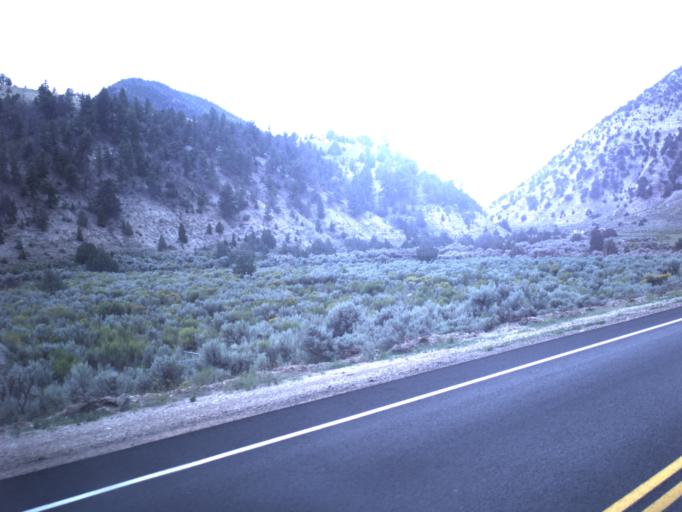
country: US
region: Utah
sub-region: Duchesne County
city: Duchesne
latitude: 39.9720
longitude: -110.6273
